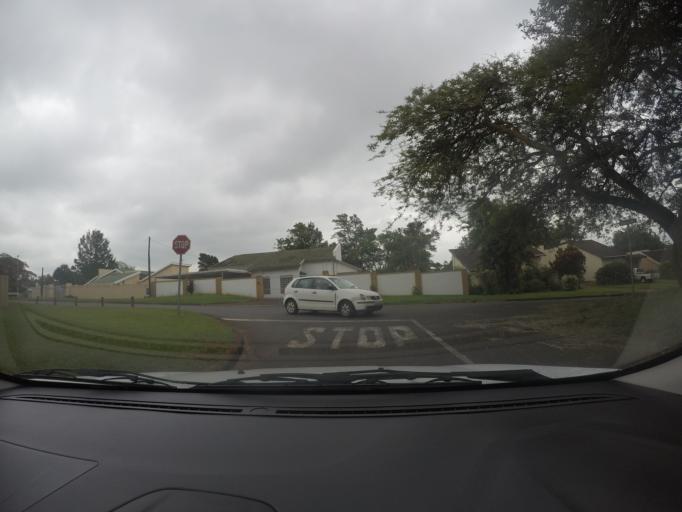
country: ZA
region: KwaZulu-Natal
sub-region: uThungulu District Municipality
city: Empangeni
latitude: -28.7627
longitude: 31.8973
